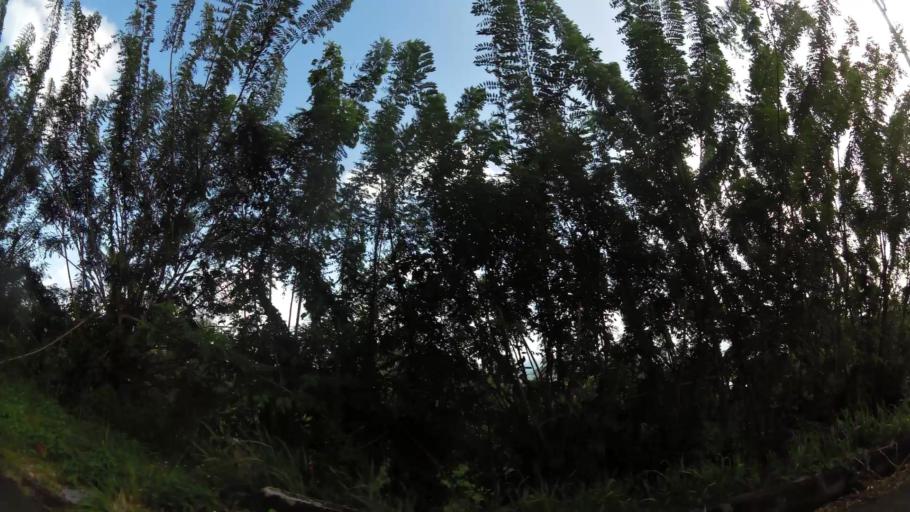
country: MQ
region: Martinique
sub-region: Martinique
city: Sainte-Marie
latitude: 14.7664
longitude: -60.9827
